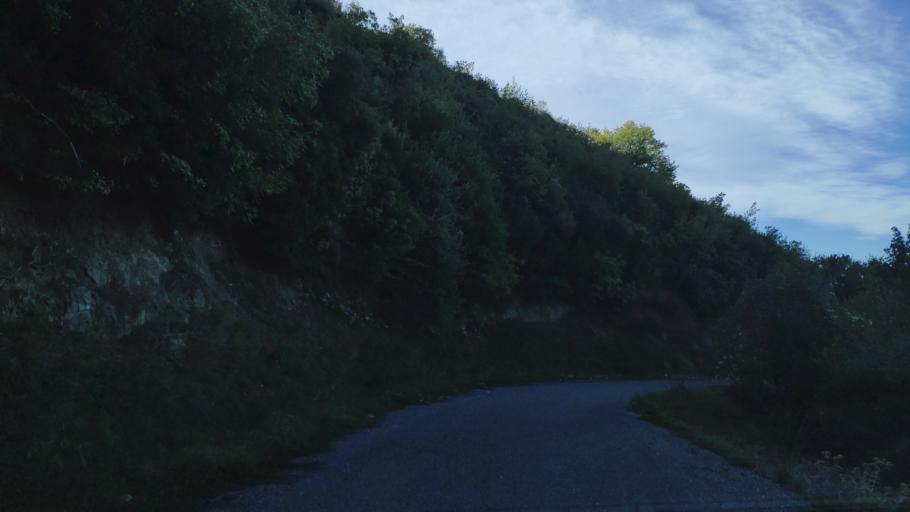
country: GR
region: Peloponnese
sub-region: Nomos Arkadias
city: Dimitsana
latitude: 37.5490
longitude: 22.0600
